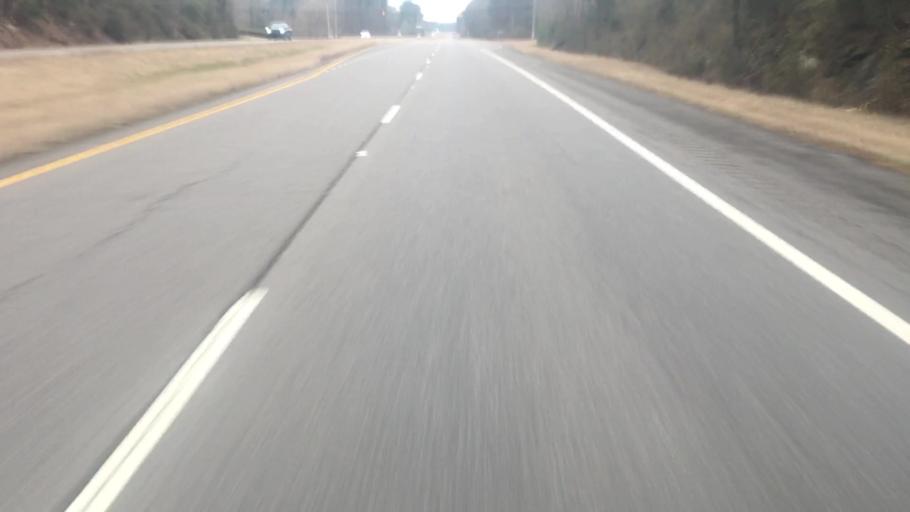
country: US
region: Alabama
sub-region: Walker County
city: Cordova
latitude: 33.8212
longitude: -87.1836
